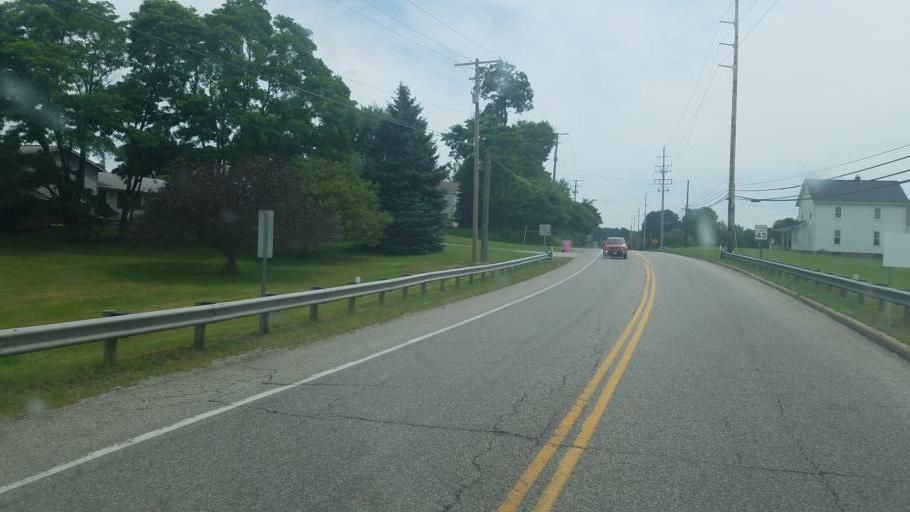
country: US
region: Ohio
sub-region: Geauga County
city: Bainbridge
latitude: 41.3883
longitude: -81.2784
